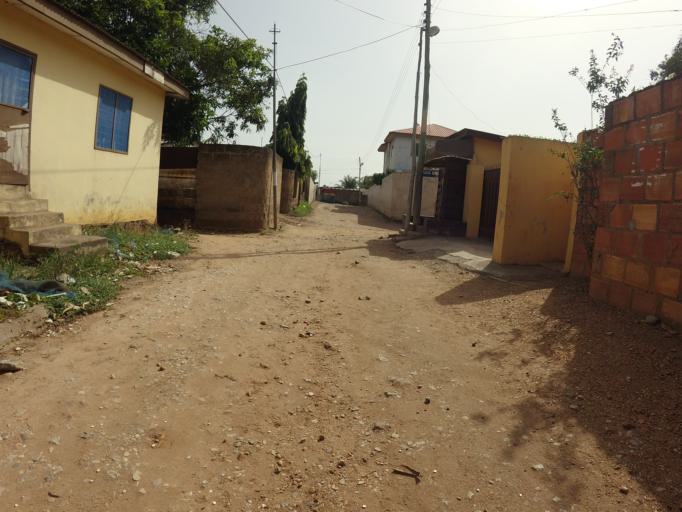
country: GH
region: Greater Accra
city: Dome
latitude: 5.6109
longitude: -0.2415
